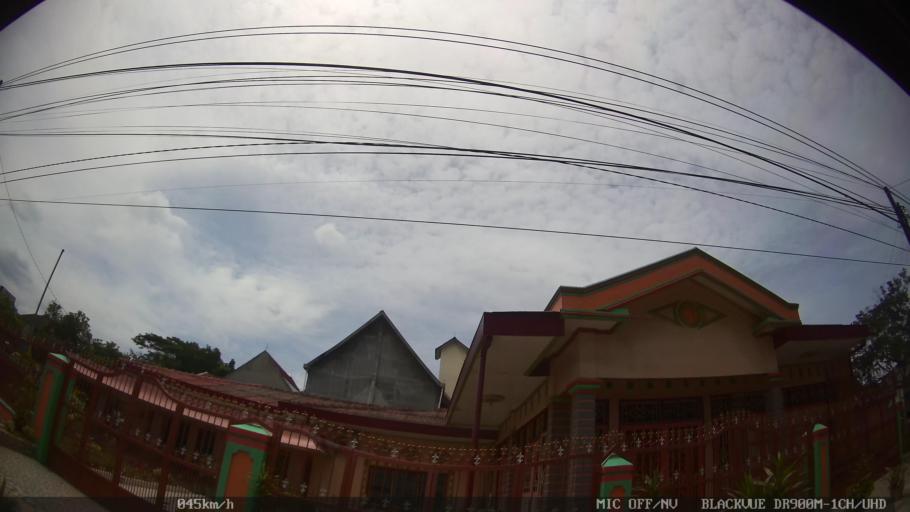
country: ID
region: North Sumatra
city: Medan
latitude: 3.5550
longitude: 98.6561
